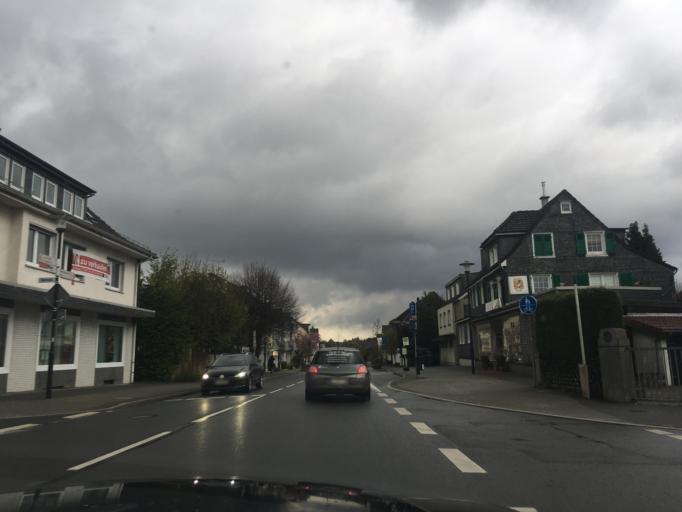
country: DE
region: North Rhine-Westphalia
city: Burscheid
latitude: 51.1041
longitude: 7.1579
